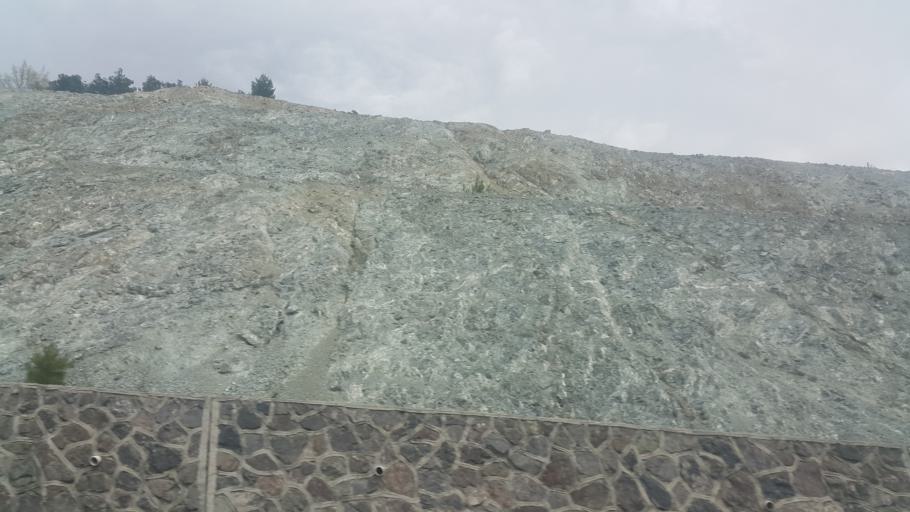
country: TR
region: Adana
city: Pozanti
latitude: 37.4324
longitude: 34.8816
